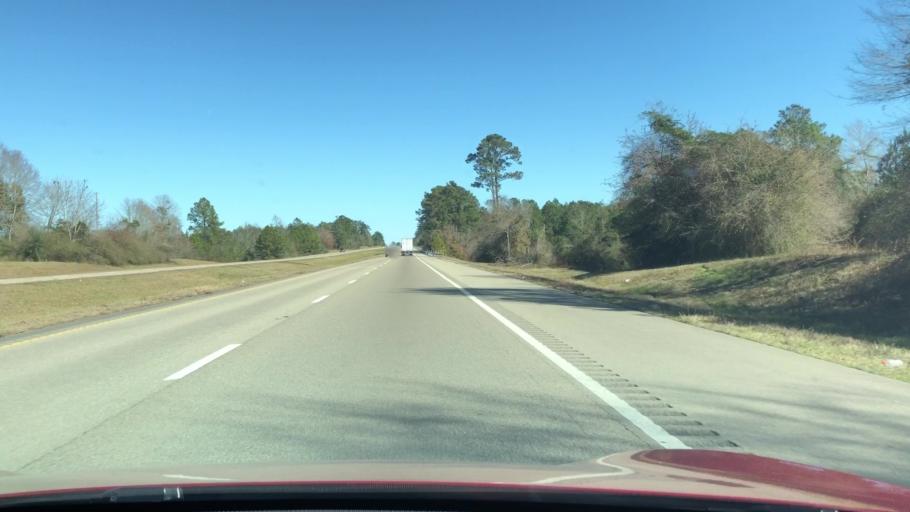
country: US
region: Mississippi
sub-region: Pearl River County
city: Poplarville
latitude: 30.7343
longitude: -89.5411
